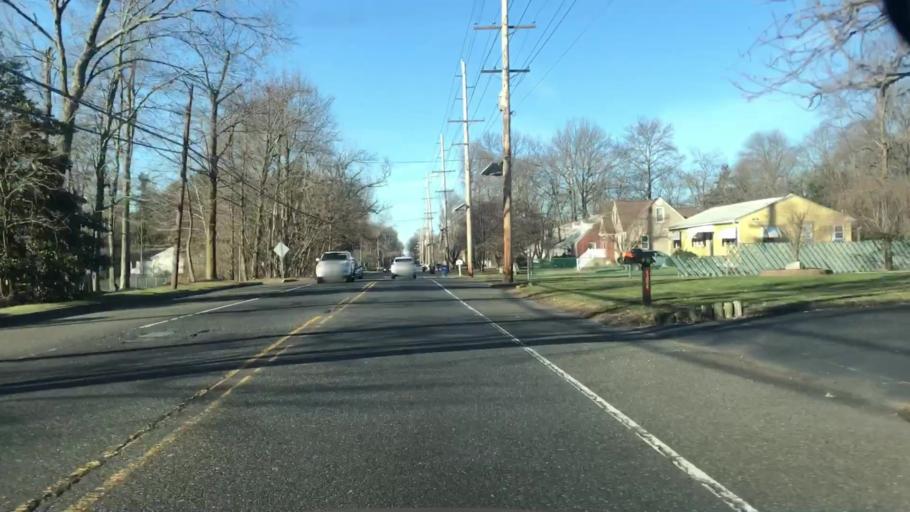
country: US
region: New Jersey
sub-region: Burlington County
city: Burlington
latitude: 40.0506
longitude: -74.8448
